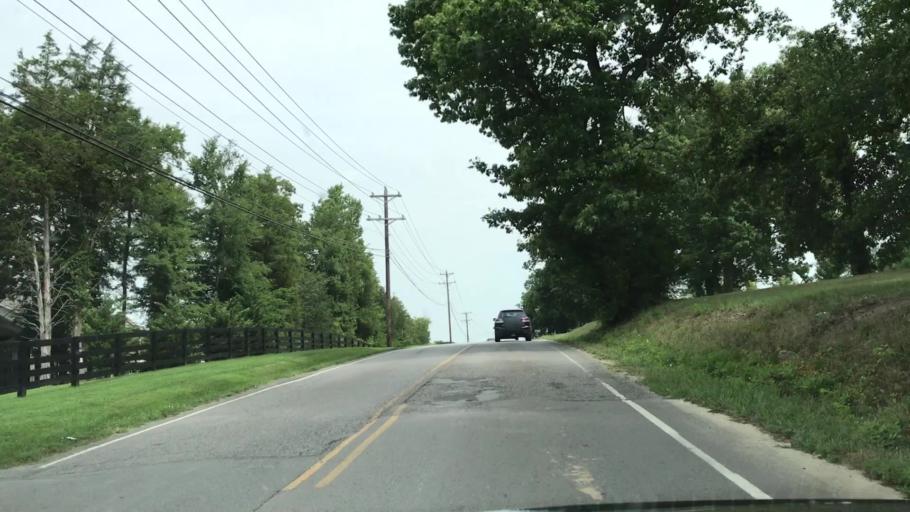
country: US
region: Tennessee
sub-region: Williamson County
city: Nolensville
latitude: 35.9438
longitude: -86.6737
